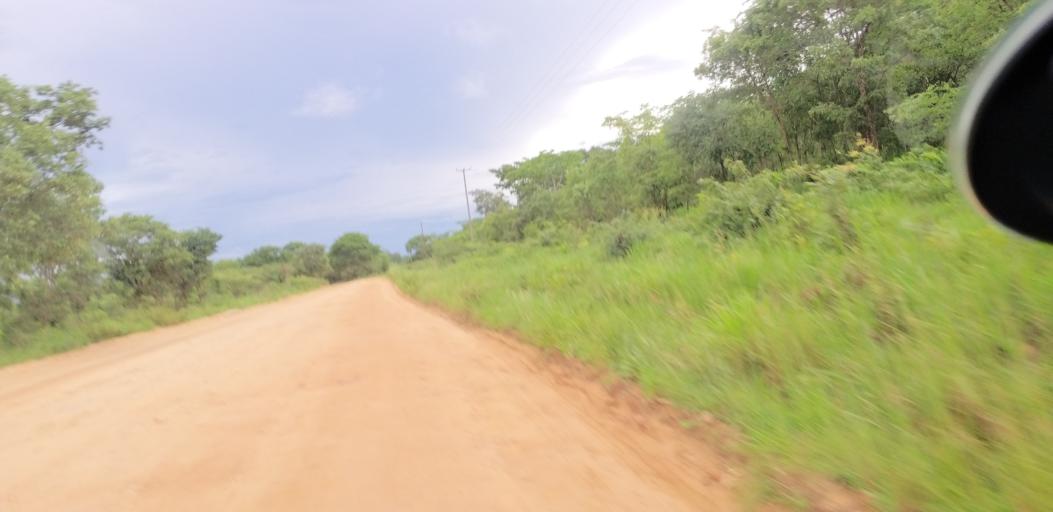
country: ZM
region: Lusaka
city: Chongwe
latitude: -15.1794
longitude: 28.4536
